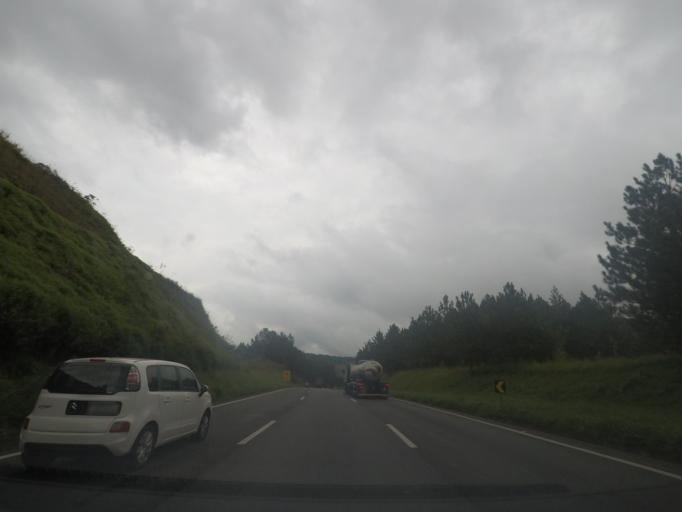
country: BR
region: Sao Paulo
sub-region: Cajati
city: Cajati
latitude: -24.9713
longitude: -48.5006
